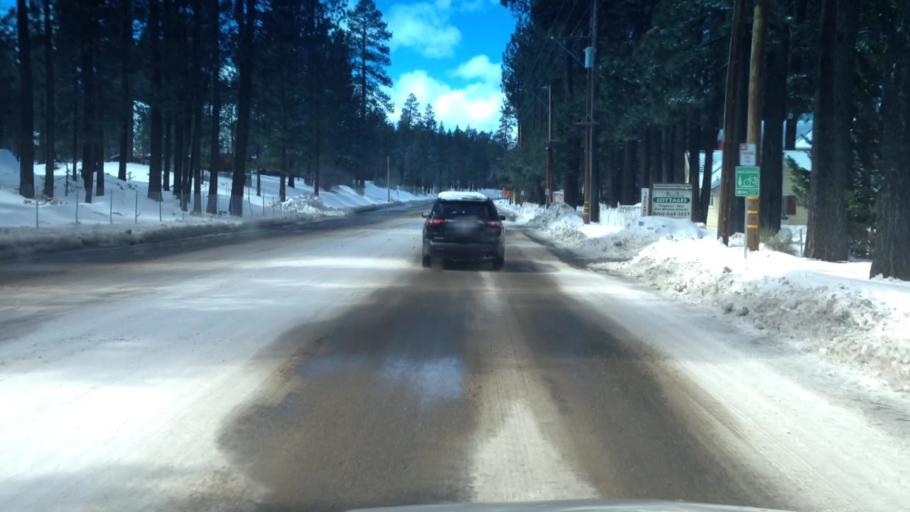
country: US
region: California
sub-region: San Bernardino County
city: Big Bear Lake
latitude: 34.2410
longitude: -116.8760
